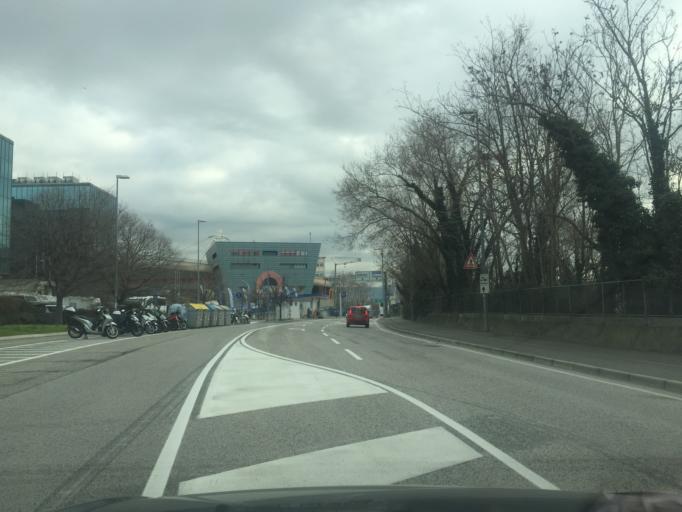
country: IT
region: Friuli Venezia Giulia
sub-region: Provincia di Trieste
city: Trieste
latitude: 45.6399
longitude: 13.7586
